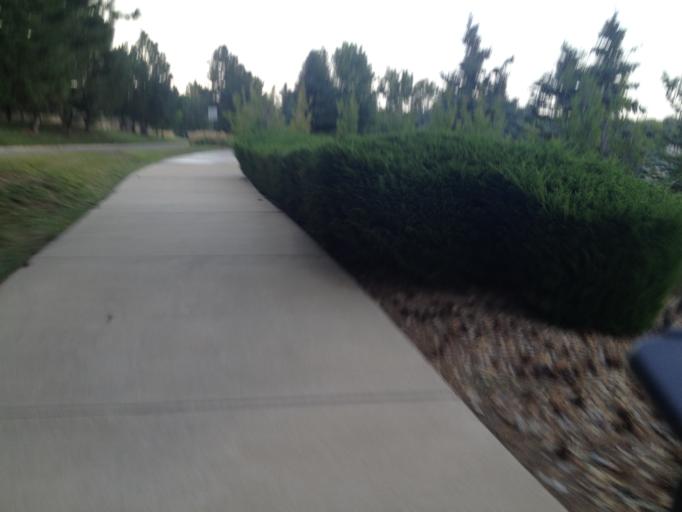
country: US
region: Colorado
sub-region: Boulder County
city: Superior
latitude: 39.9339
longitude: -105.1372
